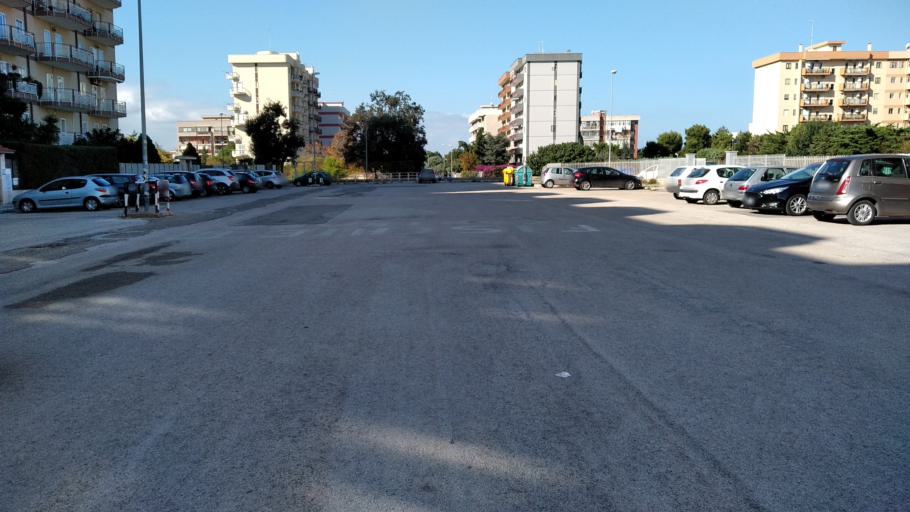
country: IT
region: Apulia
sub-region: Provincia di Bari
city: Triggiano
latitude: 41.1059
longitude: 16.9098
